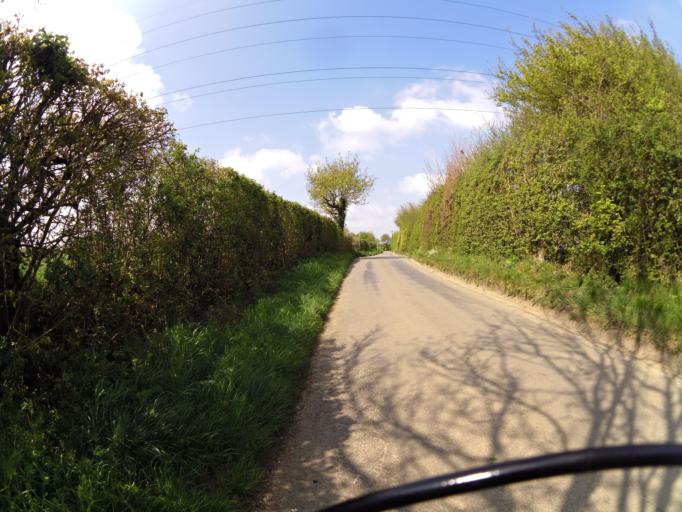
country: GB
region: England
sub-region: Suffolk
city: Bramford
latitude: 52.0829
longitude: 1.0660
